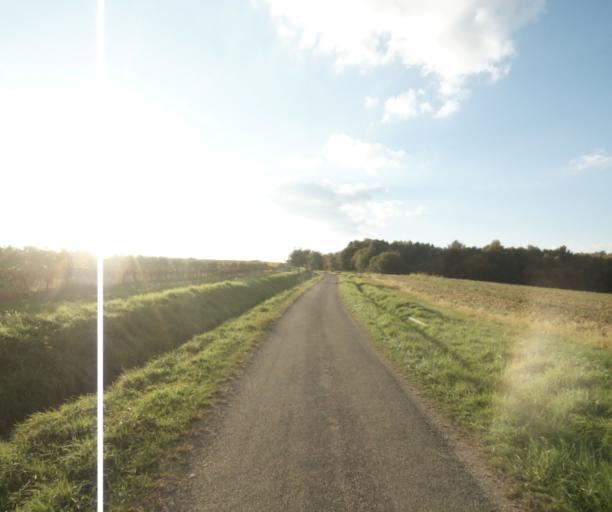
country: FR
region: Midi-Pyrenees
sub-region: Departement du Gers
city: Eauze
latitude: 43.7566
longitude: 0.1483
